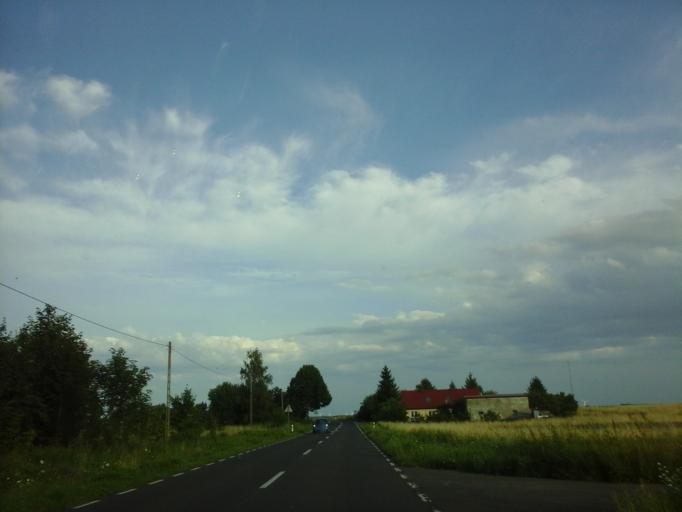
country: PL
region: West Pomeranian Voivodeship
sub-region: Powiat kamienski
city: Kamien Pomorski
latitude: 53.9346
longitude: 14.8187
